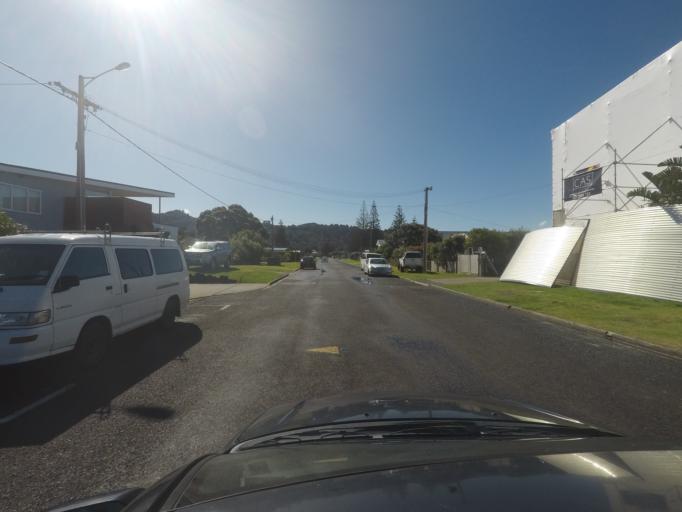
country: NZ
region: Bay of Plenty
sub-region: Western Bay of Plenty District
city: Waihi Beach
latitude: -37.4055
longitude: 175.9428
